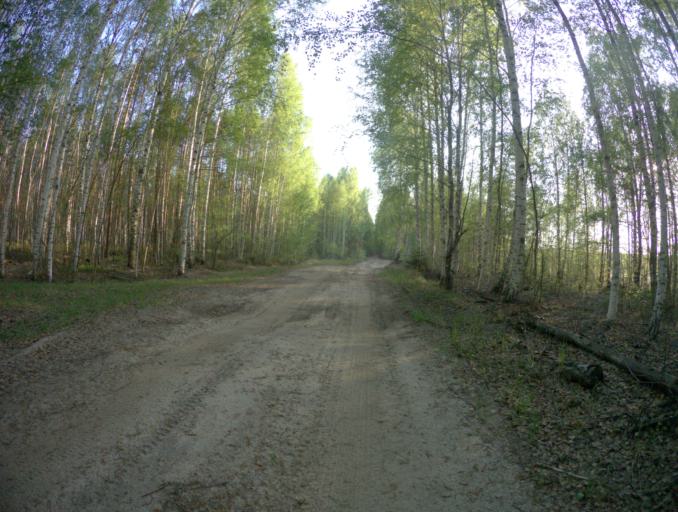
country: RU
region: Vladimir
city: Vyazniki
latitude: 56.3670
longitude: 42.1550
